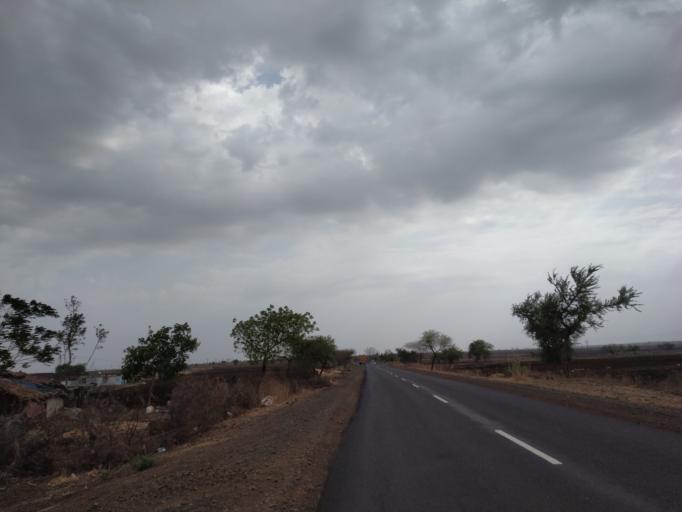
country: IN
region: Madhya Pradesh
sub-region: Shajapur
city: Susner
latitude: 24.0356
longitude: 76.1416
